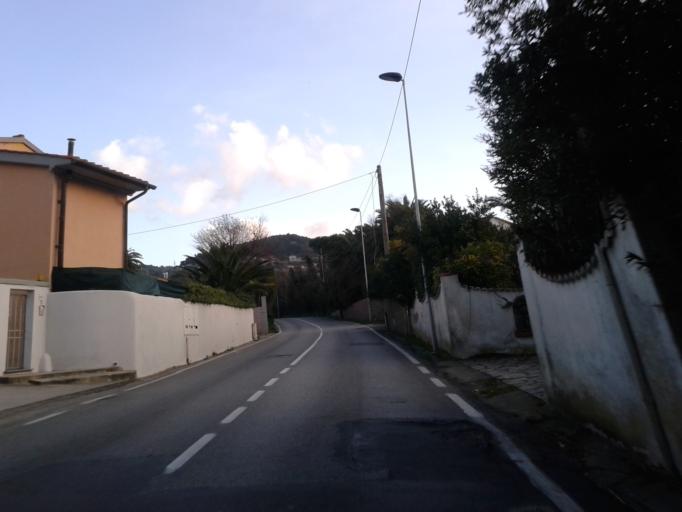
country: IT
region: Tuscany
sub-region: Provincia di Livorno
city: Livorno
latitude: 43.5018
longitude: 10.3405
